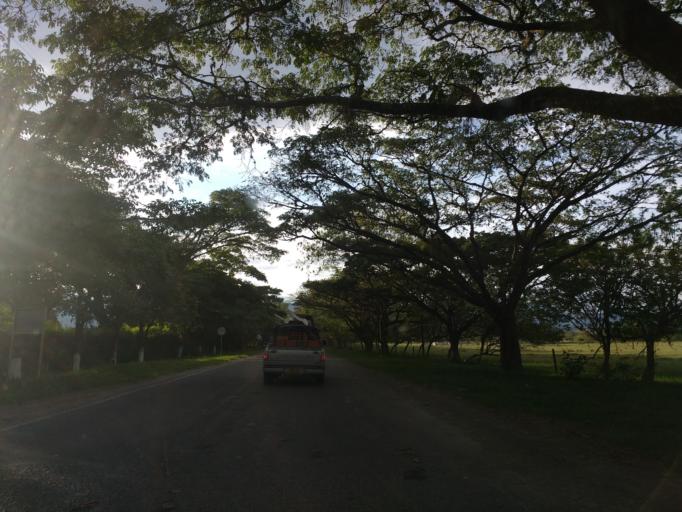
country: CO
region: Valle del Cauca
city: Ansermanuevo
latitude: 4.7720
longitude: -75.9575
